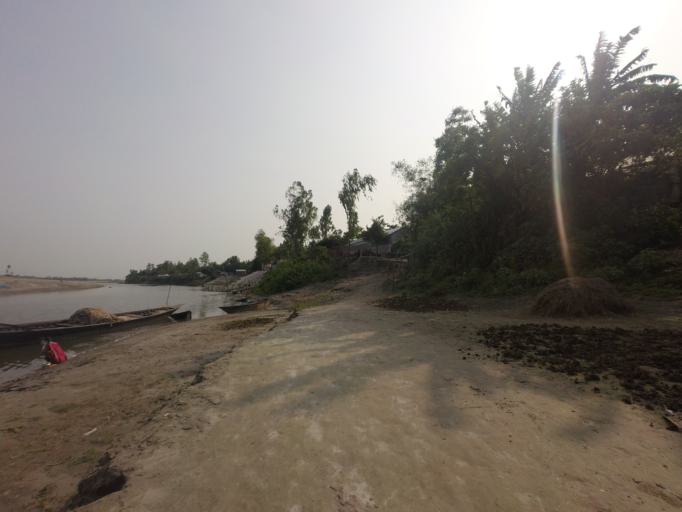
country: BD
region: Rajshahi
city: Sirajganj
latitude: 24.3328
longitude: 89.7151
